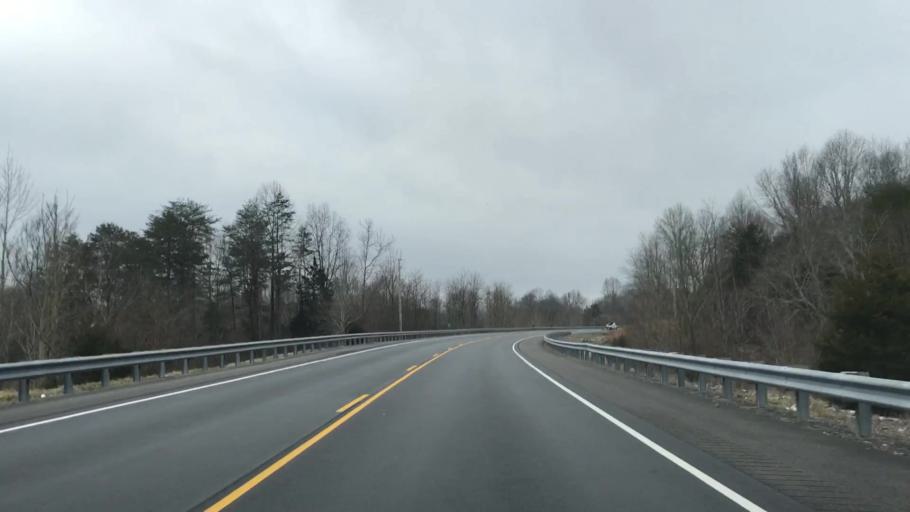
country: US
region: Kentucky
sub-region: Adair County
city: Columbia
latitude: 36.9747
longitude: -85.4207
